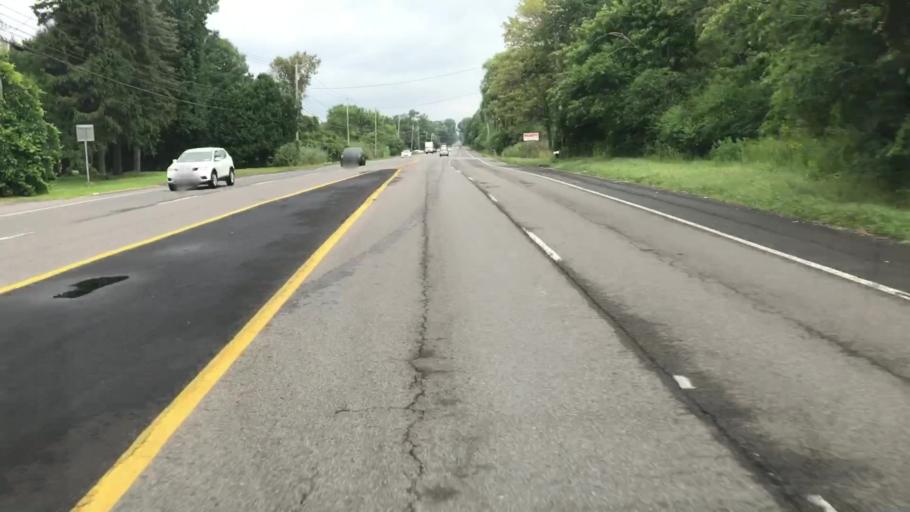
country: US
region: New York
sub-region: Onondaga County
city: Liverpool
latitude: 43.1430
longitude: -76.2069
